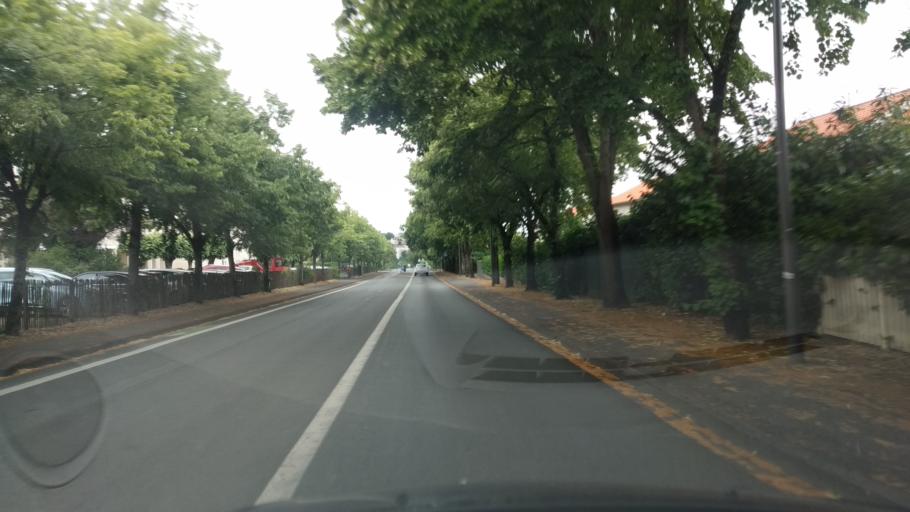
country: FR
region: Poitou-Charentes
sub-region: Departement de la Vienne
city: Poitiers
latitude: 46.5921
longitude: 0.3488
